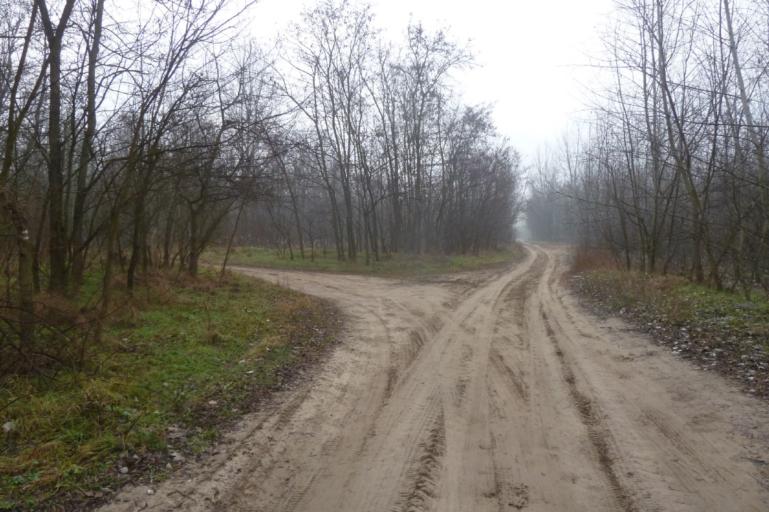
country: HU
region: Pest
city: Tapioszentmarton
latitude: 47.3545
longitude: 19.7464
